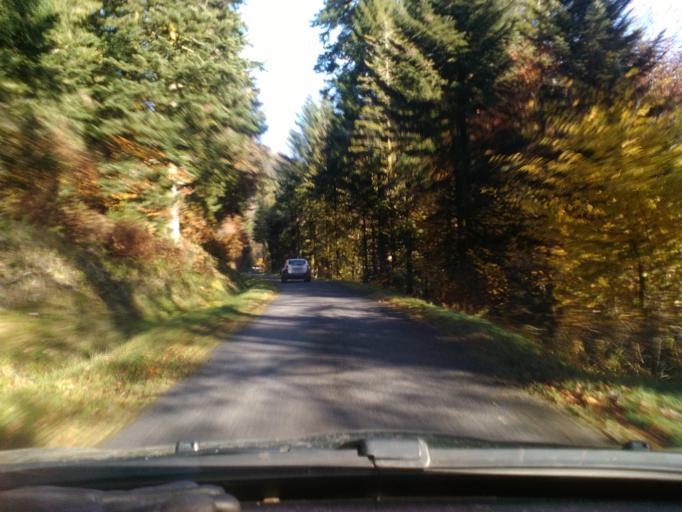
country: FR
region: Lorraine
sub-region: Departement des Vosges
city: Senones
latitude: 48.4481
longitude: 7.0482
